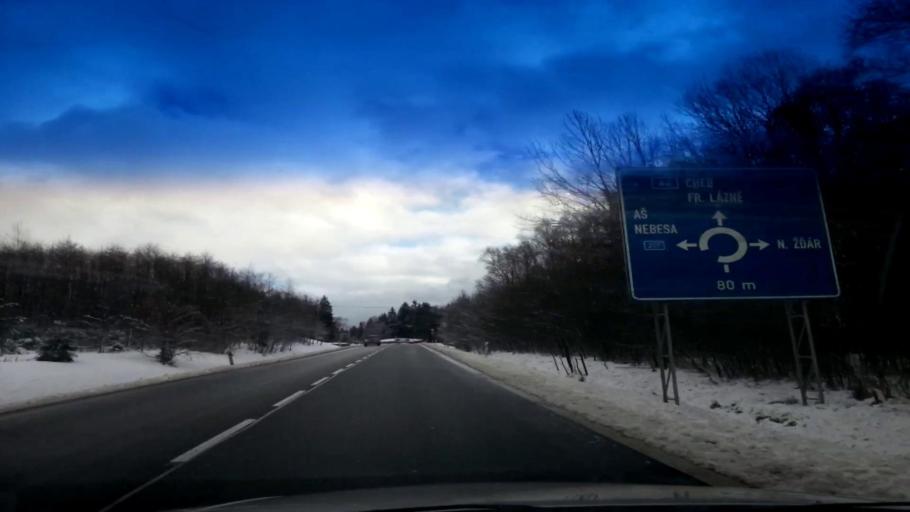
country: CZ
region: Karlovarsky
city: As
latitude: 50.1949
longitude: 12.2140
